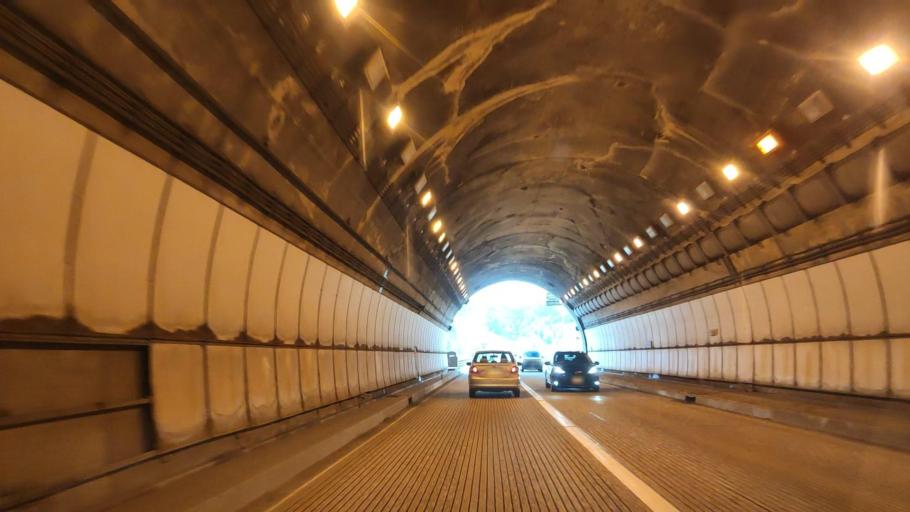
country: JP
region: Akita
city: Takanosu
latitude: 40.2186
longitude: 140.2530
